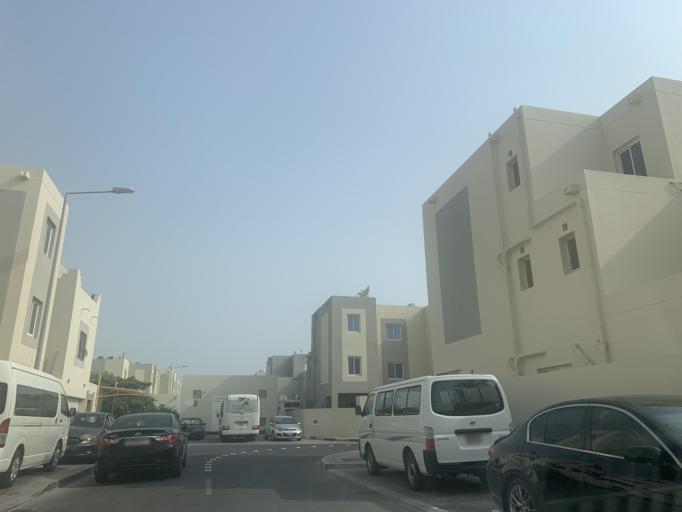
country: BH
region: Manama
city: Jidd Hafs
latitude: 26.2332
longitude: 50.4549
